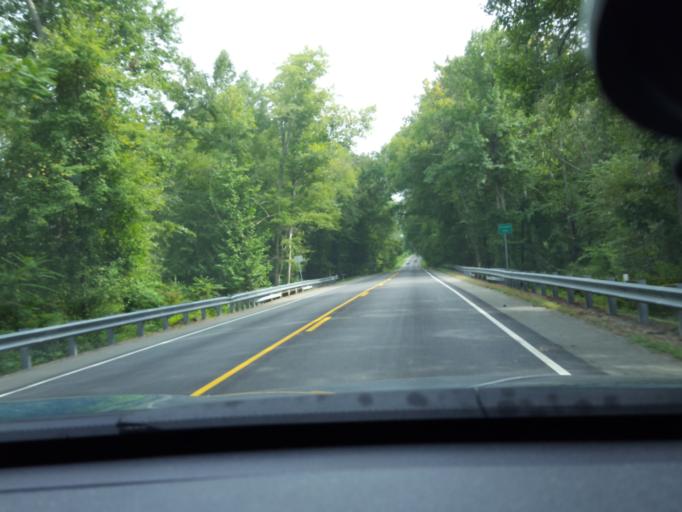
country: US
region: Virginia
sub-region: Hanover County
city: Hanover
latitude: 37.7588
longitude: -77.3646
